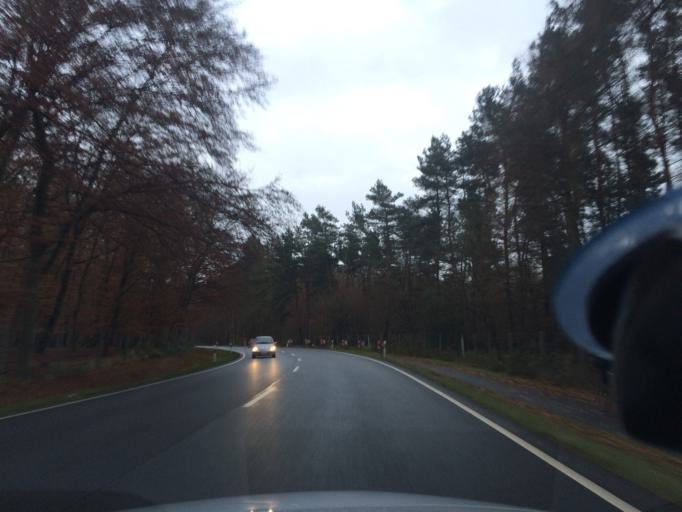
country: DE
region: Hesse
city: Morfelden-Walldorf
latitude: 49.9743
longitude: 8.5277
